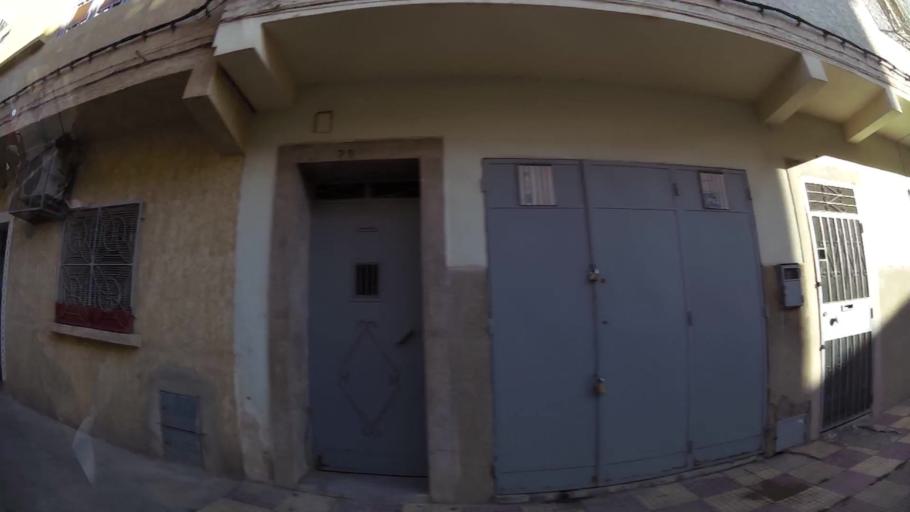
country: MA
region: Oriental
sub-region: Oujda-Angad
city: Oujda
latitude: 34.6975
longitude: -1.9044
